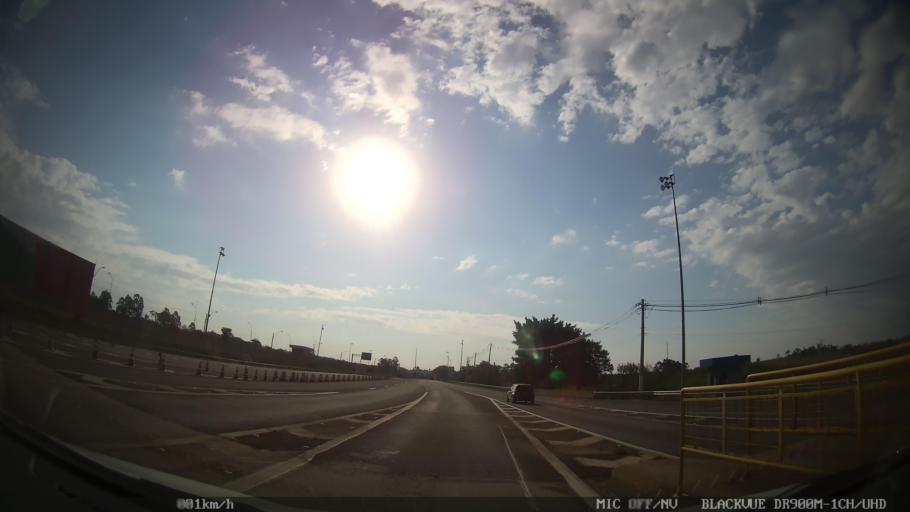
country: BR
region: Sao Paulo
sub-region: Cosmopolis
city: Cosmopolis
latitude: -22.6895
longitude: -47.1553
